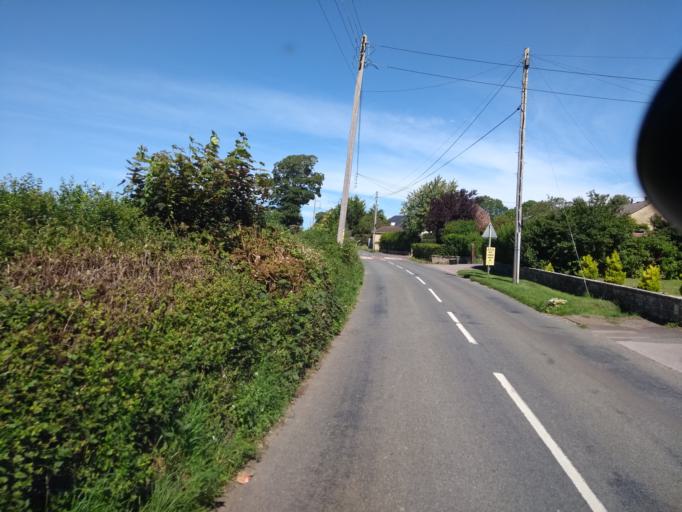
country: GB
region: England
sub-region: Somerset
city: Ilchester
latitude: 51.0601
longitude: -2.6740
